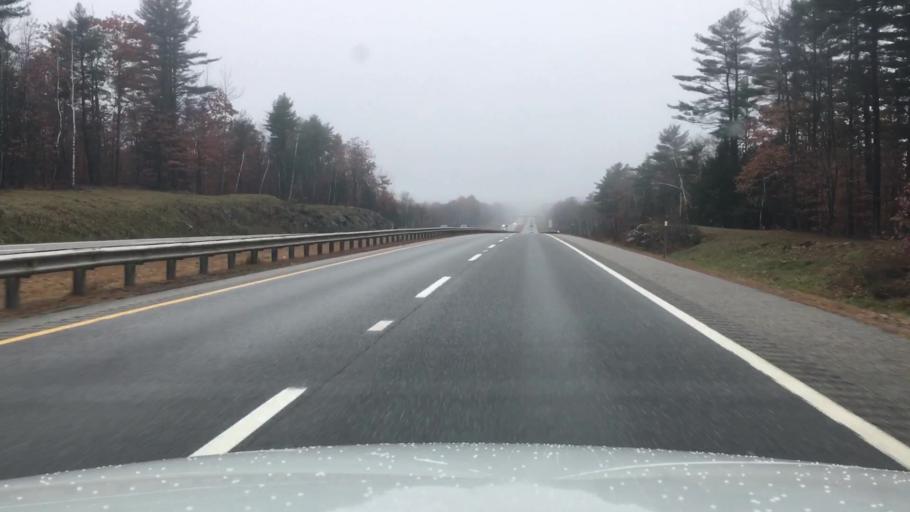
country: US
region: Maine
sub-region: Androscoggin County
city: Sabattus
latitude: 44.1247
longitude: -70.0028
